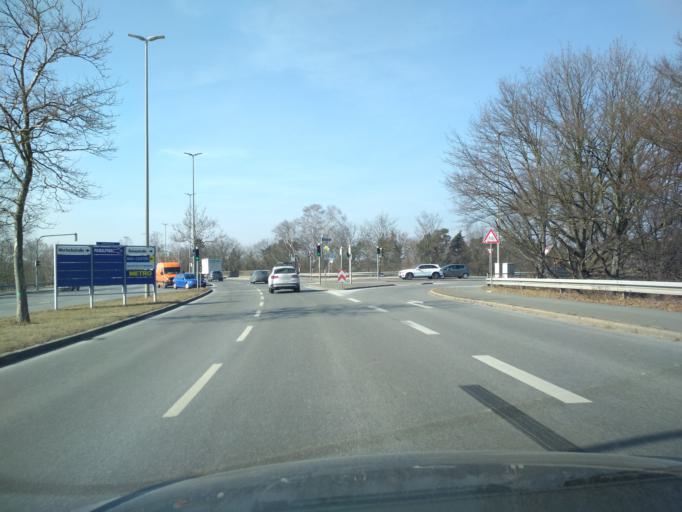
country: DE
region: Bavaria
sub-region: Regierungsbezirk Mittelfranken
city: Stein
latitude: 49.4083
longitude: 11.0497
